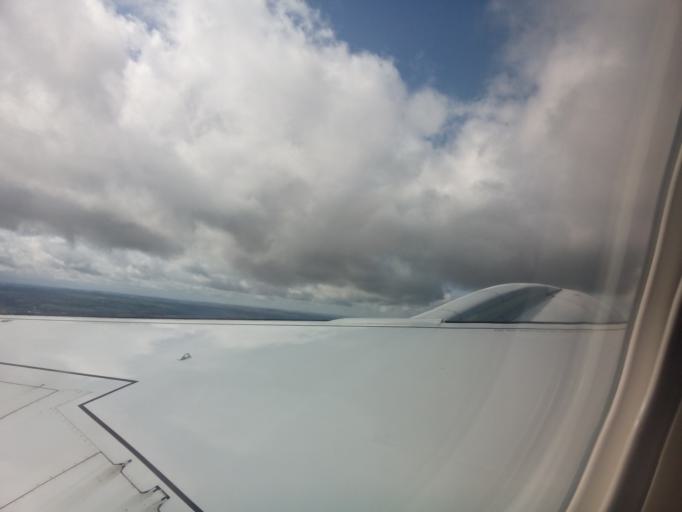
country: GB
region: England
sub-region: Northumberland
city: Ponteland
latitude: 55.0323
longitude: -1.7124
